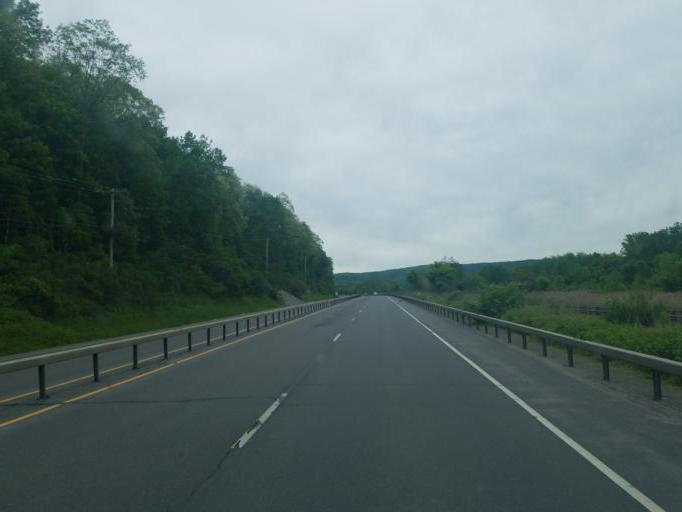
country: US
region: New York
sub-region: Herkimer County
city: Ilion
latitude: 43.0201
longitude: -75.0243
